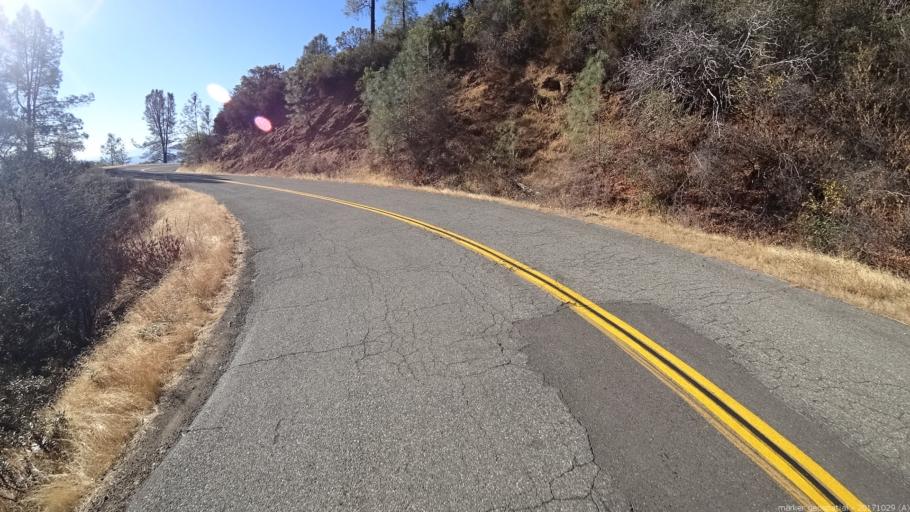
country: US
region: California
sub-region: Trinity County
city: Lewiston
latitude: 40.3839
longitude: -122.8419
